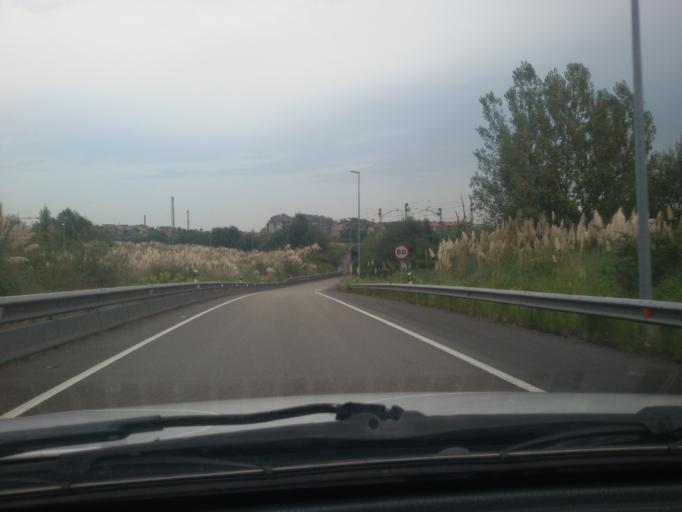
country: ES
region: Asturias
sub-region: Province of Asturias
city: Lugones
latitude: 43.3989
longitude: -5.8206
